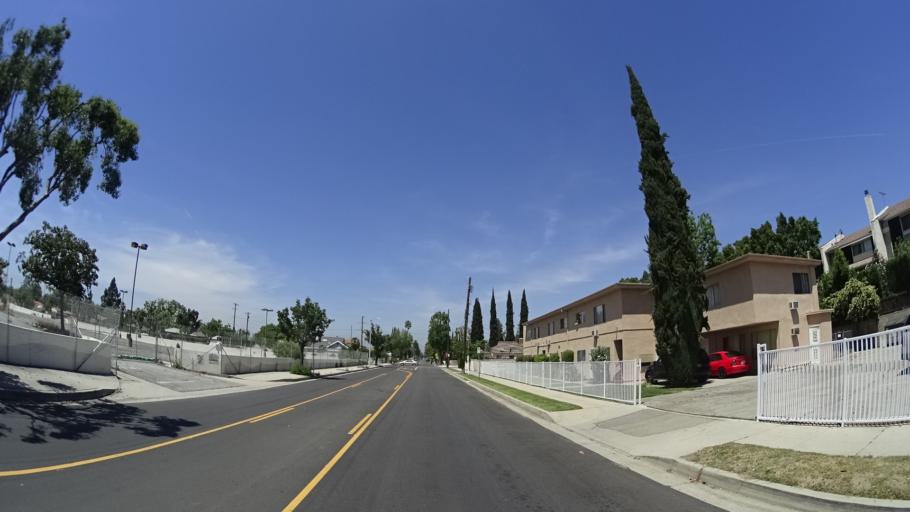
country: US
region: California
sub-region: Los Angeles County
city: North Hollywood
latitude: 34.1820
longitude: -118.3922
